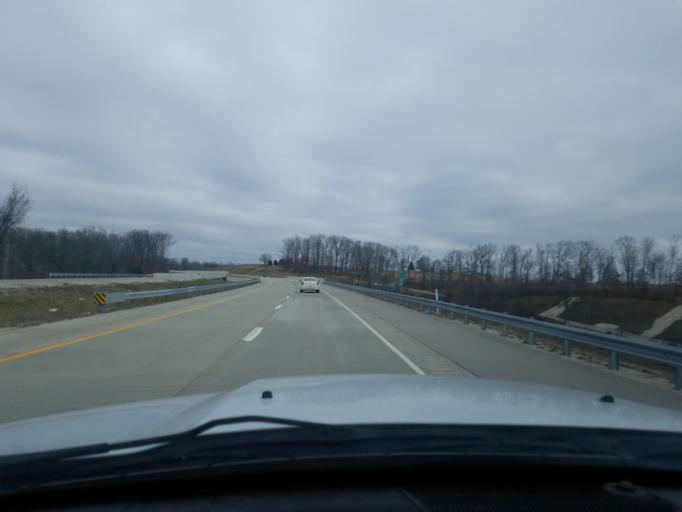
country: US
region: Indiana
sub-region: Lawrence County
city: Oolitic
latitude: 38.9837
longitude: -86.7096
